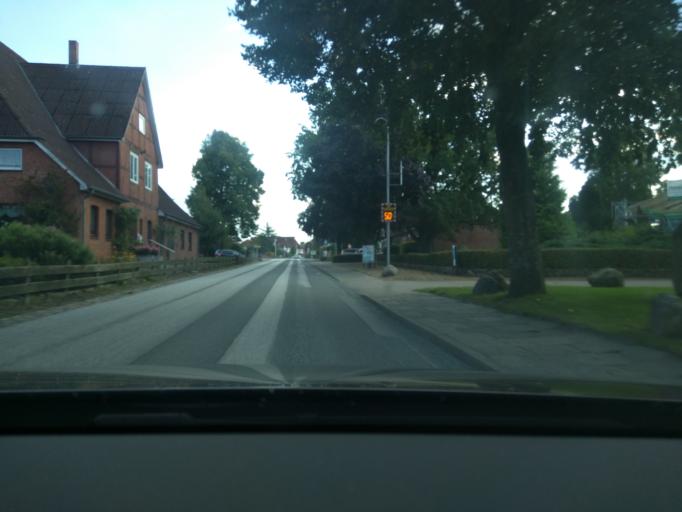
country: DE
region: Schleswig-Holstein
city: Lutau
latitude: 53.4348
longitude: 10.5495
